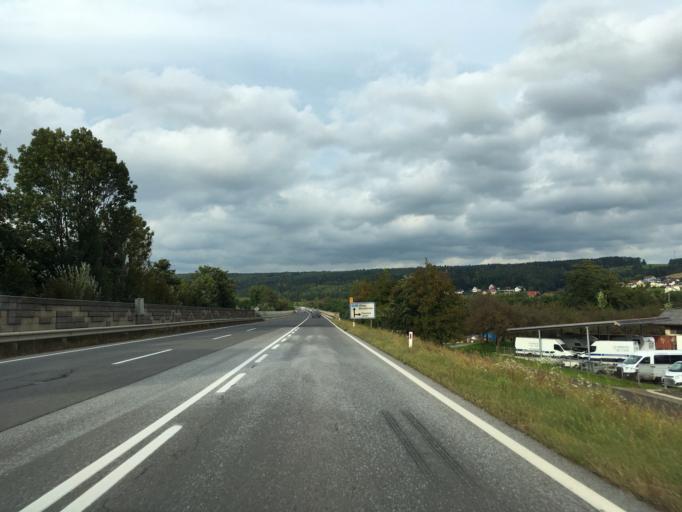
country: AT
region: Styria
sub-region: Politischer Bezirk Hartberg-Fuerstenfeld
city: Lafnitz
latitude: 47.3648
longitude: 16.0150
